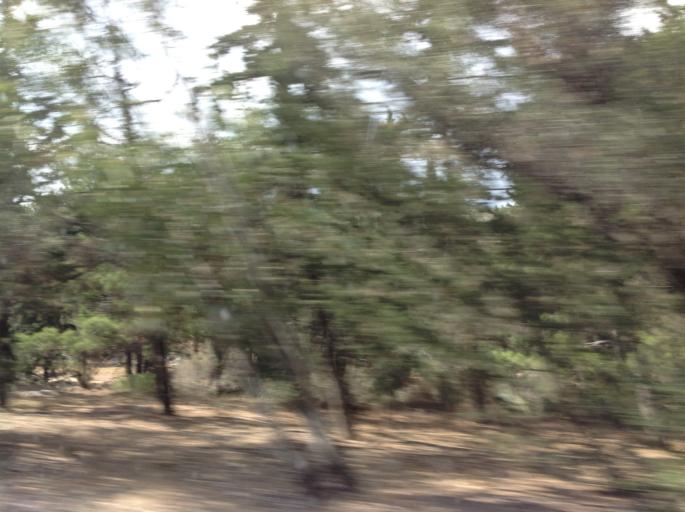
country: GR
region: Attica
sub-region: Nomos Attikis
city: Zografos
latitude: 37.9656
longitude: 23.7851
